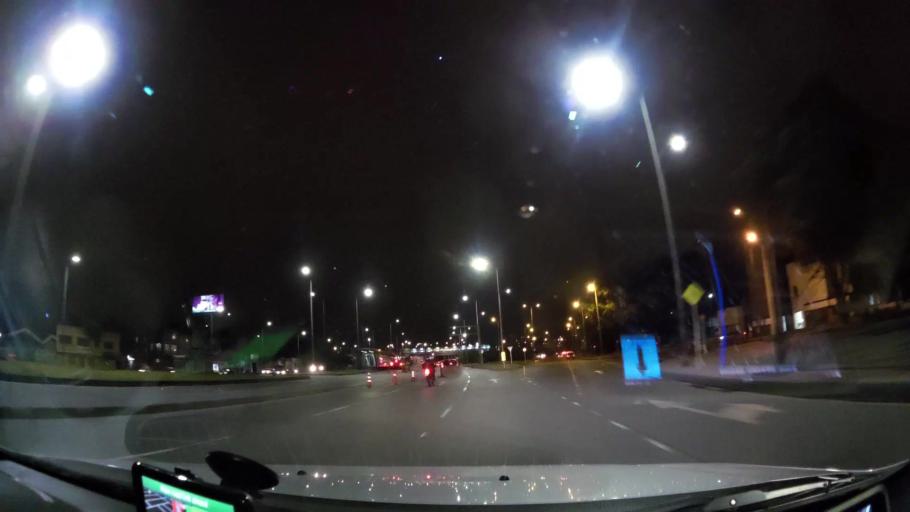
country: CO
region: Bogota D.C.
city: Bogota
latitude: 4.5935
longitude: -74.1306
